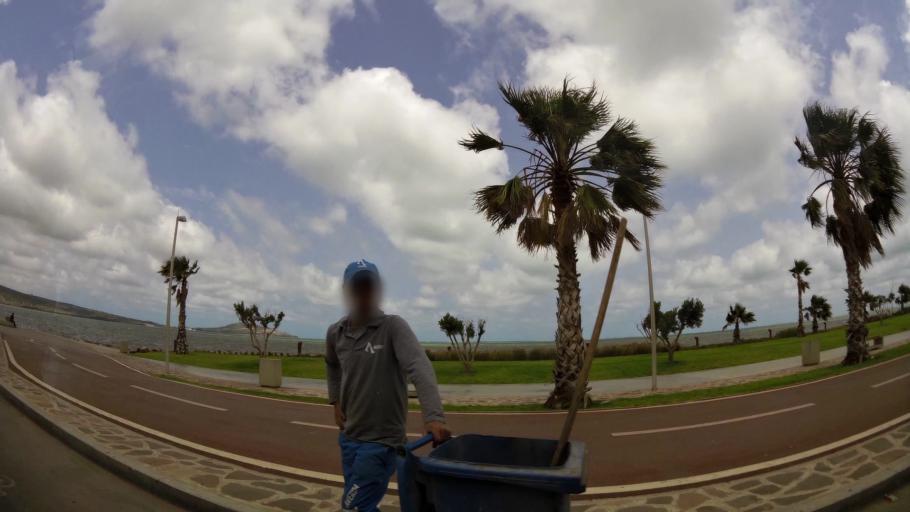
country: MA
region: Oriental
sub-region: Nador
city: Nador
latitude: 35.1775
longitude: -2.9203
